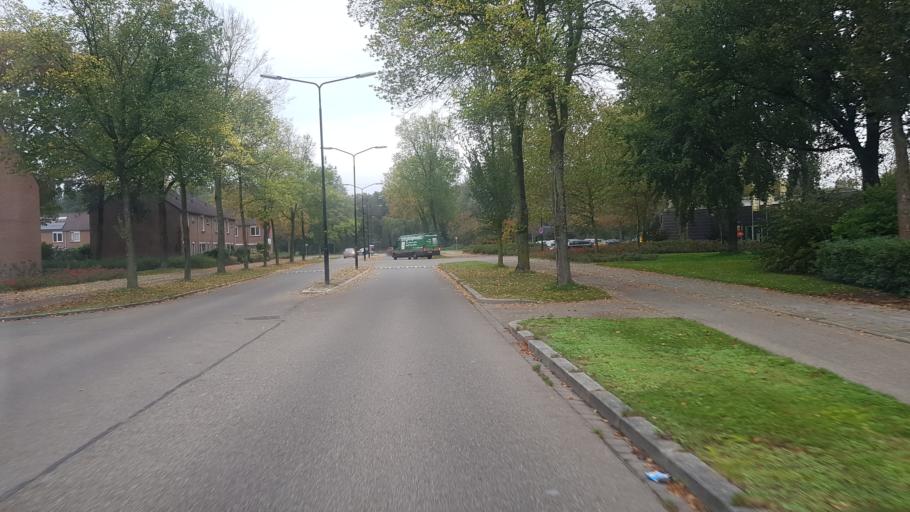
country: NL
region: Gelderland
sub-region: Gemeente Apeldoorn
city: Apeldoorn
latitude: 52.2201
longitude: 5.9924
